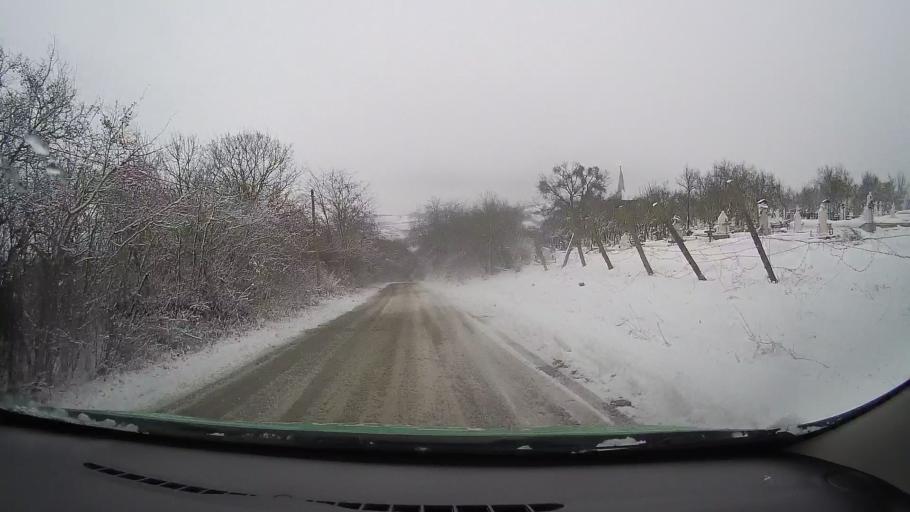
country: RO
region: Hunedoara
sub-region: Municipiul Hunedoara
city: Pestisu Mare
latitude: 45.8045
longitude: 22.9190
